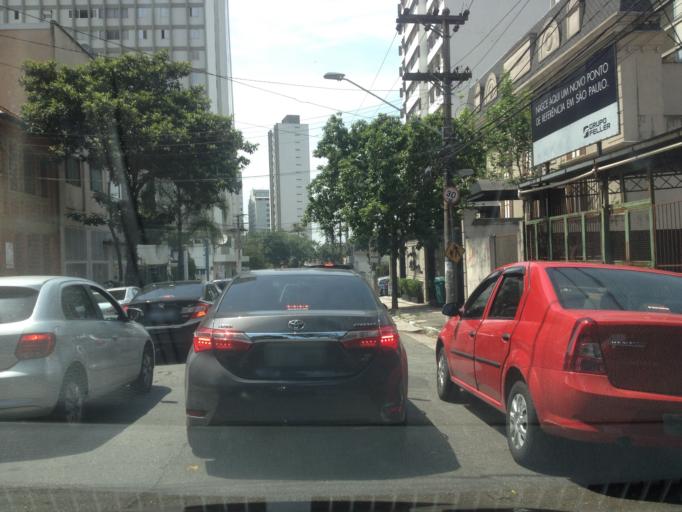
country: BR
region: Sao Paulo
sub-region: Sao Paulo
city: Sao Paulo
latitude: -23.5606
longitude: -46.6748
